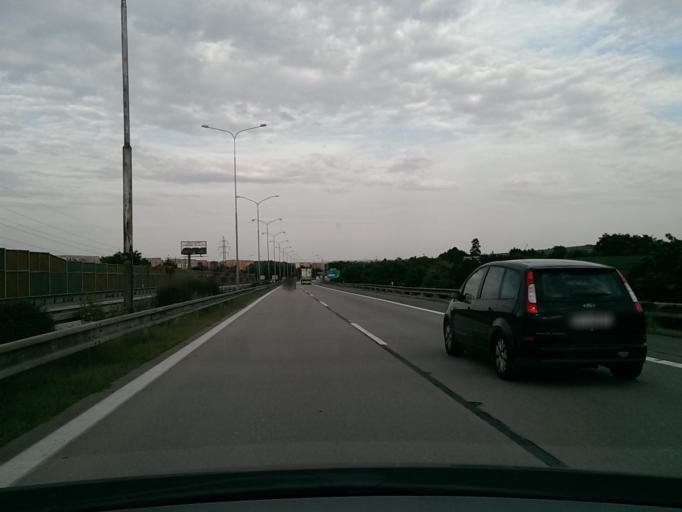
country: CZ
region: South Moravian
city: Ostopovice
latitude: 49.1697
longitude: 16.5324
